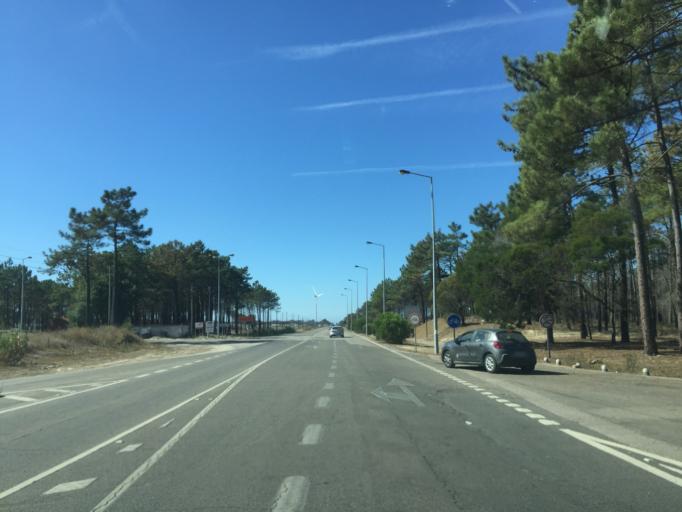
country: PT
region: Coimbra
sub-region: Mira
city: Mira
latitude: 40.3224
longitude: -8.7880
